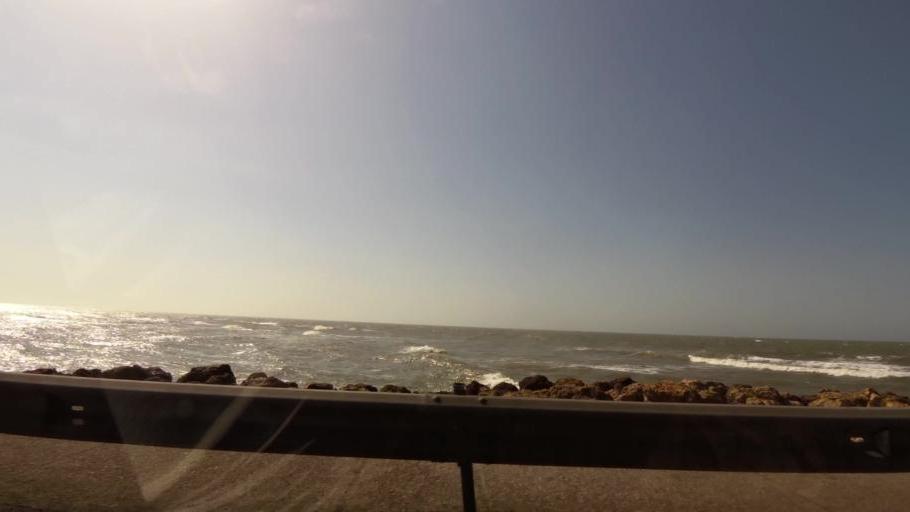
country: CO
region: Bolivar
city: Cartagena
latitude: 10.4243
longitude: -75.5546
